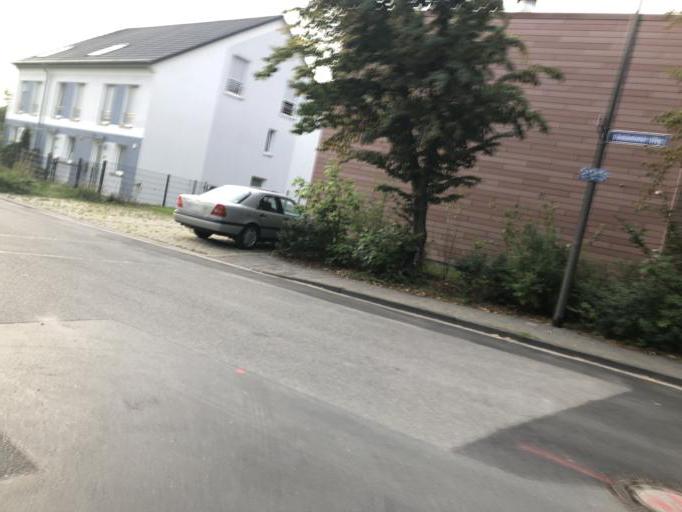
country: DE
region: Bavaria
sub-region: Regierungsbezirk Mittelfranken
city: Erlangen
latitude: 49.5768
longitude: 10.9965
